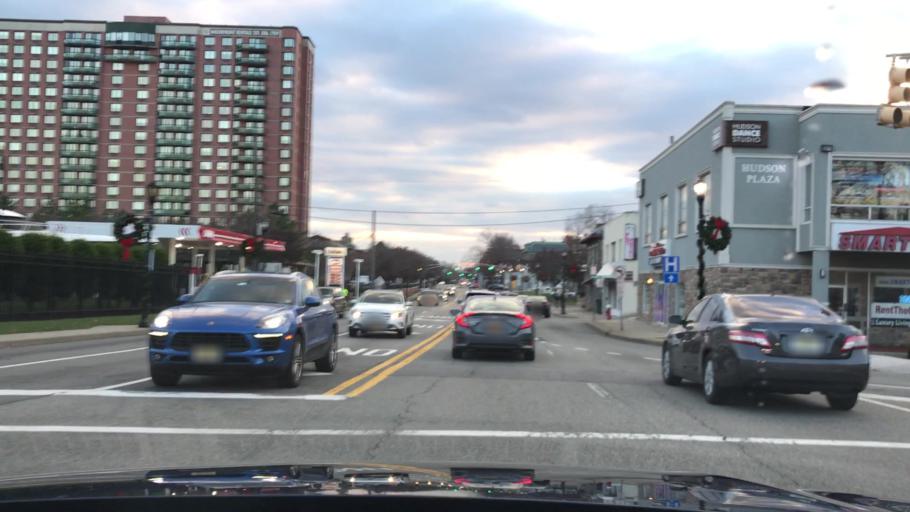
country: US
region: New Jersey
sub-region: Bergen County
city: Edgewater
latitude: 40.8289
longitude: -73.9723
